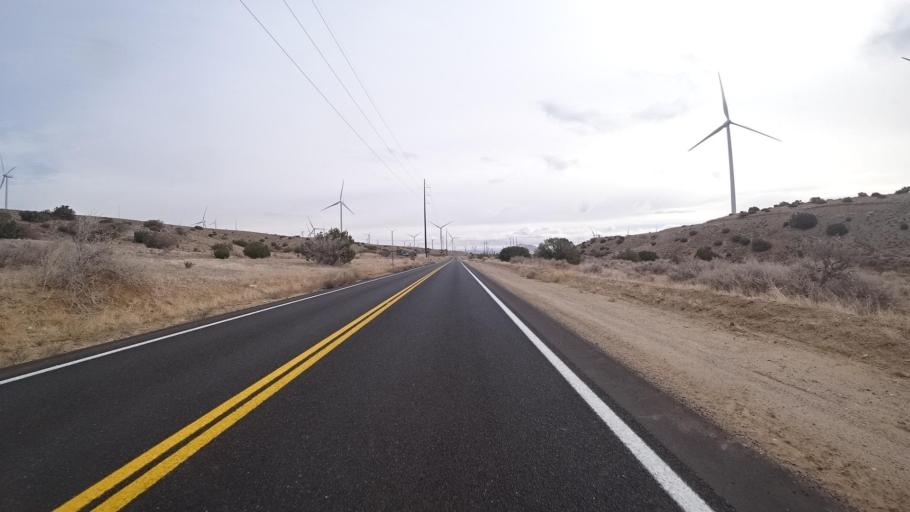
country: US
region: California
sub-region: Kern County
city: Mojave
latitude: 35.0476
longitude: -118.3202
